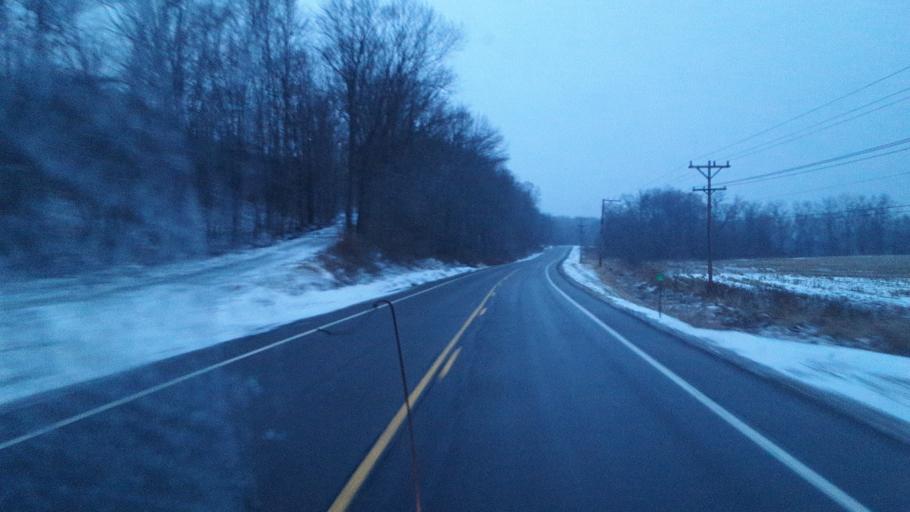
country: US
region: New York
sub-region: Allegany County
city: Belmont
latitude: 42.3035
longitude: -78.0893
